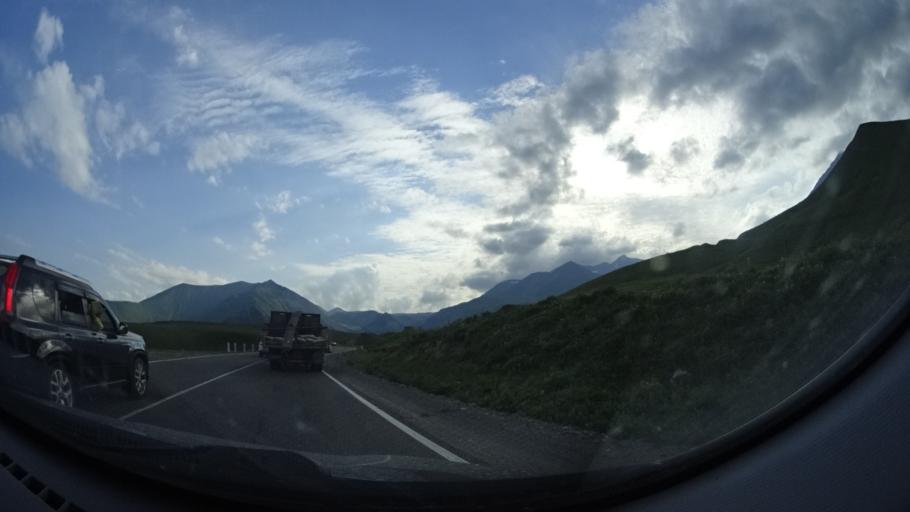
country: GE
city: Gudauri
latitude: 42.4951
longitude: 44.4618
